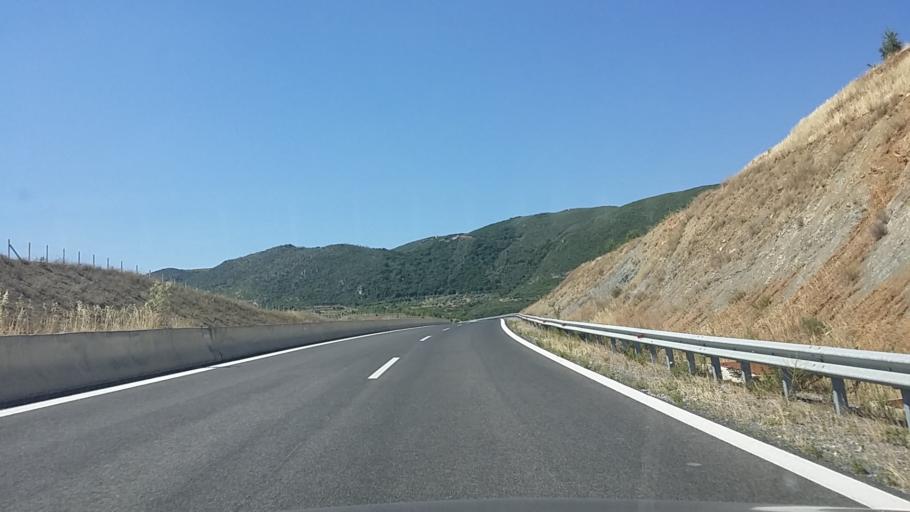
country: GR
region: Peloponnese
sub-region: Nomos Arkadias
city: Megalopoli
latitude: 37.3158
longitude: 22.1709
